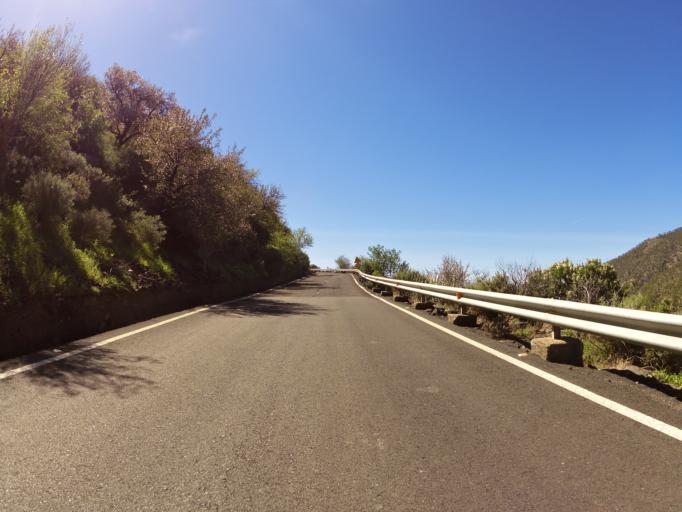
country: ES
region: Canary Islands
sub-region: Provincia de Las Palmas
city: Artenara
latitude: 28.0112
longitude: -15.6883
